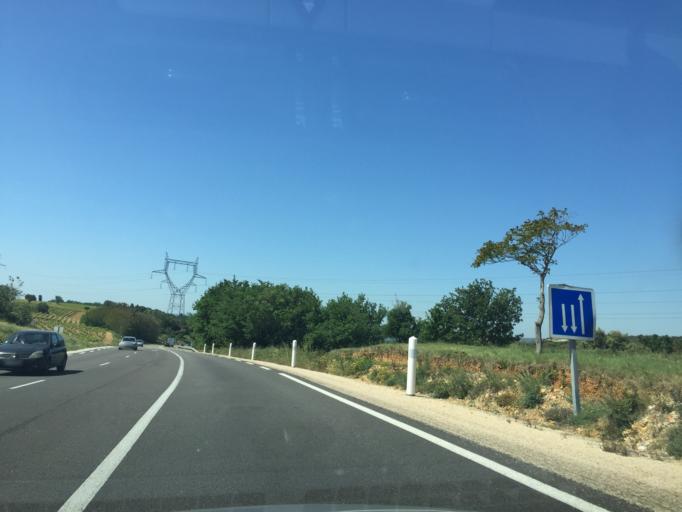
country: FR
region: Languedoc-Roussillon
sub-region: Departement du Gard
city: Saze
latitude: 43.9470
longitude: 4.6274
